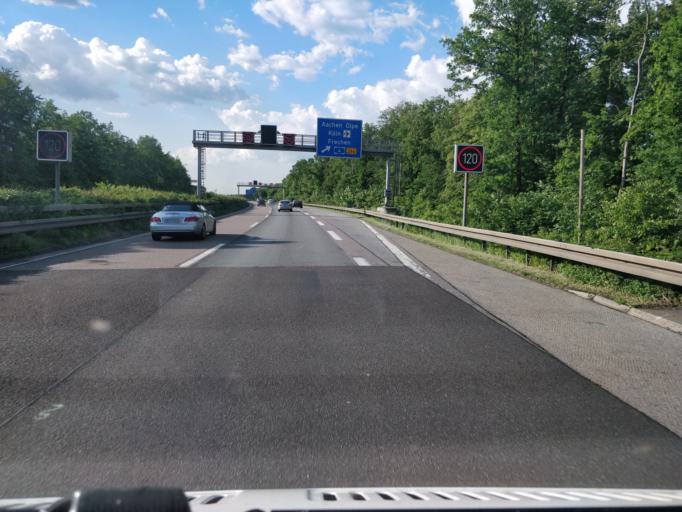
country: DE
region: North Rhine-Westphalia
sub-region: Regierungsbezirk Koln
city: Frechen
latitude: 50.9121
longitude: 6.8470
